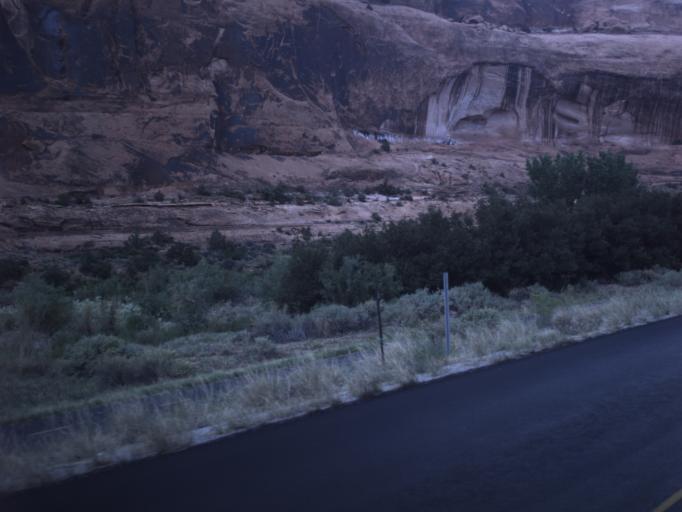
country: US
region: Utah
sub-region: Grand County
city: Moab
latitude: 38.6129
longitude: -109.5560
